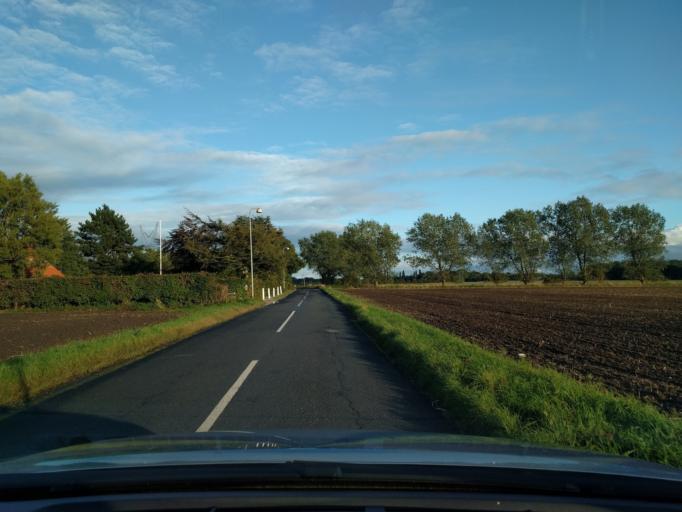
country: DK
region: South Denmark
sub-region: Odense Kommune
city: Bullerup
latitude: 55.4256
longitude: 10.4967
